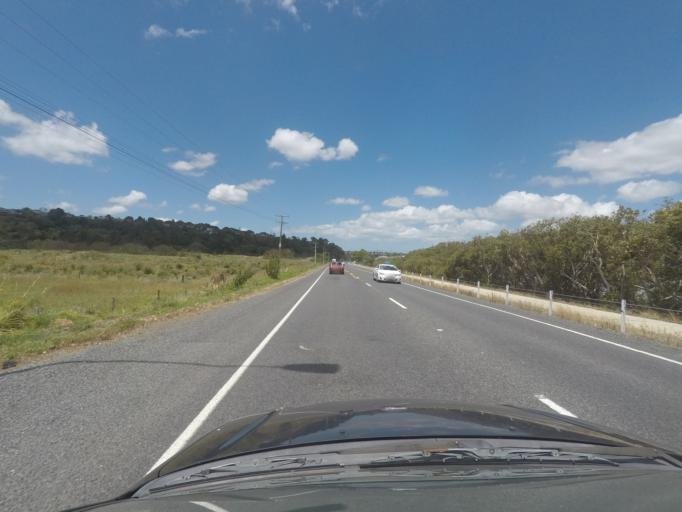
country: NZ
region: Northland
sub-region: Whangarei
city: Whangarei
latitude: -35.7326
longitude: 174.3464
